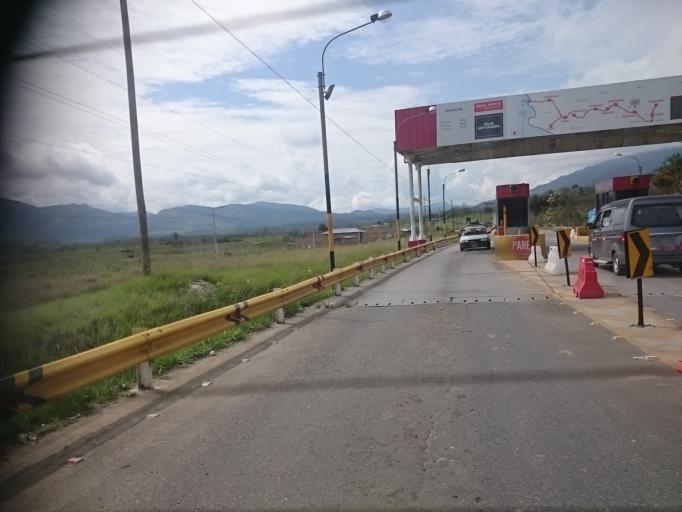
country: PE
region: San Martin
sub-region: Provincia de Moyobamba
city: Moyobamba
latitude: -6.0537
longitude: -76.9380
